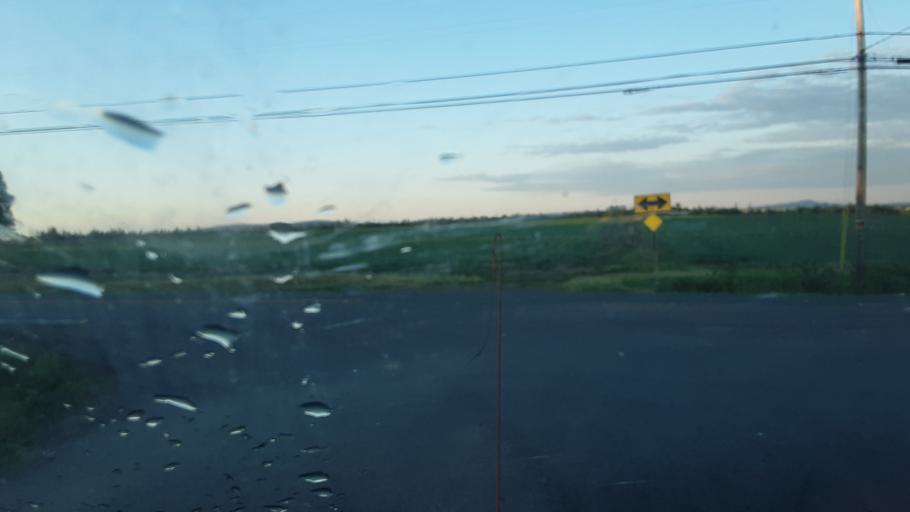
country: US
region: Maine
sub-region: Aroostook County
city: Caribou
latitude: 46.8027
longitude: -68.1349
